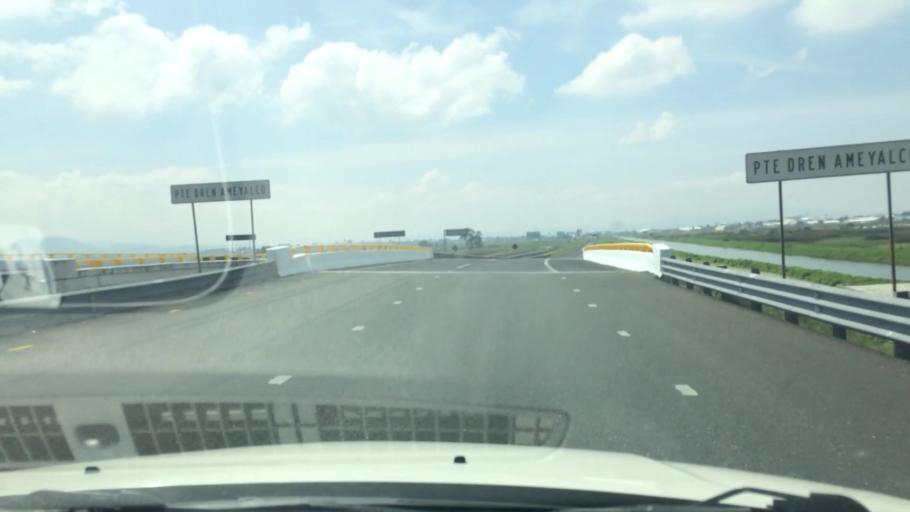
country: MX
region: Mexico
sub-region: Lerma
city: Colonia Isidro Fabela
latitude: 19.3184
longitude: -99.5212
